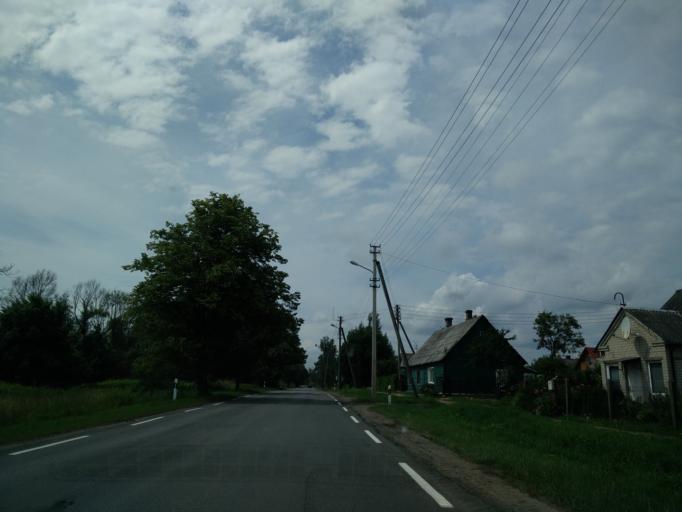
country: LT
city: Skaidiskes
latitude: 54.6930
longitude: 25.4564
